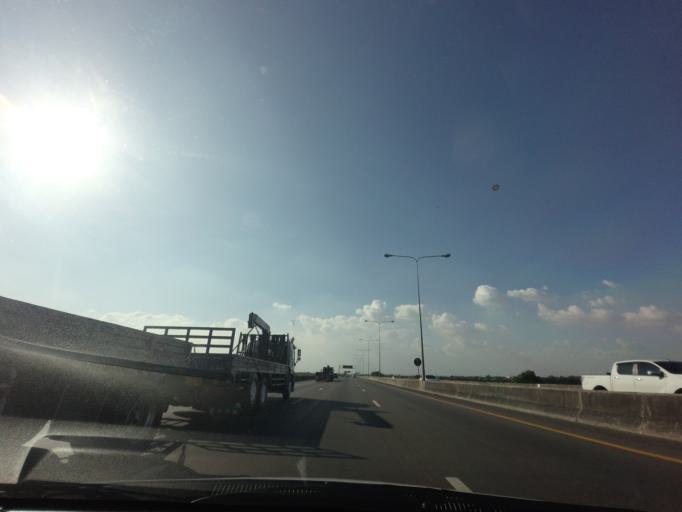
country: TH
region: Samut Prakan
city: Samut Prakan
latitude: 13.6012
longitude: 100.6385
